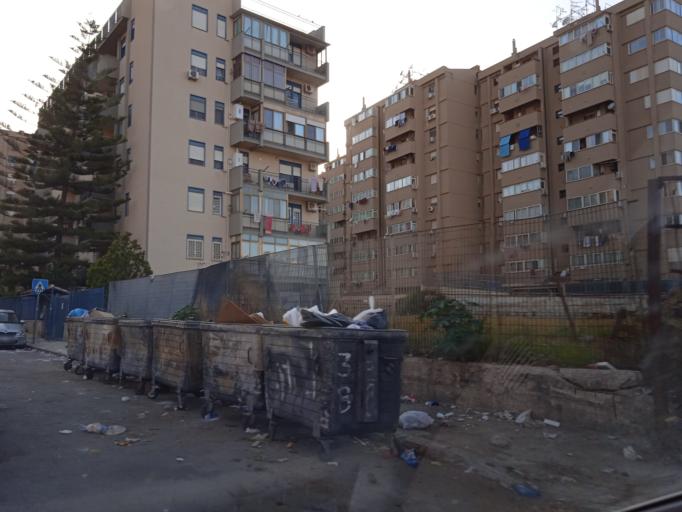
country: IT
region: Sicily
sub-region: Palermo
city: Ciaculli
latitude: 38.0853
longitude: 13.3635
